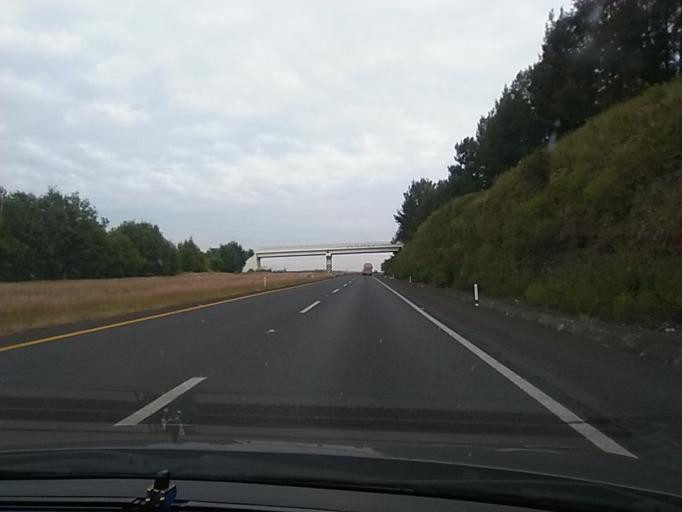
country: MX
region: Michoacan
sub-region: Puruandiro
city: San Lorenzo
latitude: 19.9607
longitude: -101.6762
